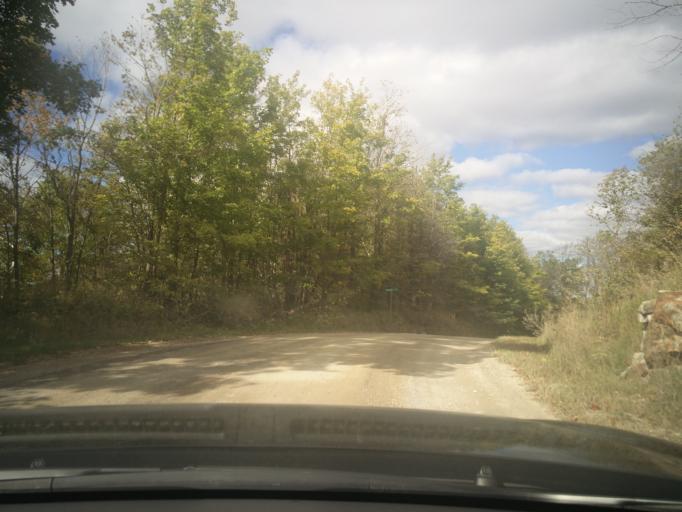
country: CA
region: Ontario
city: Perth
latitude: 44.6598
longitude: -76.5786
